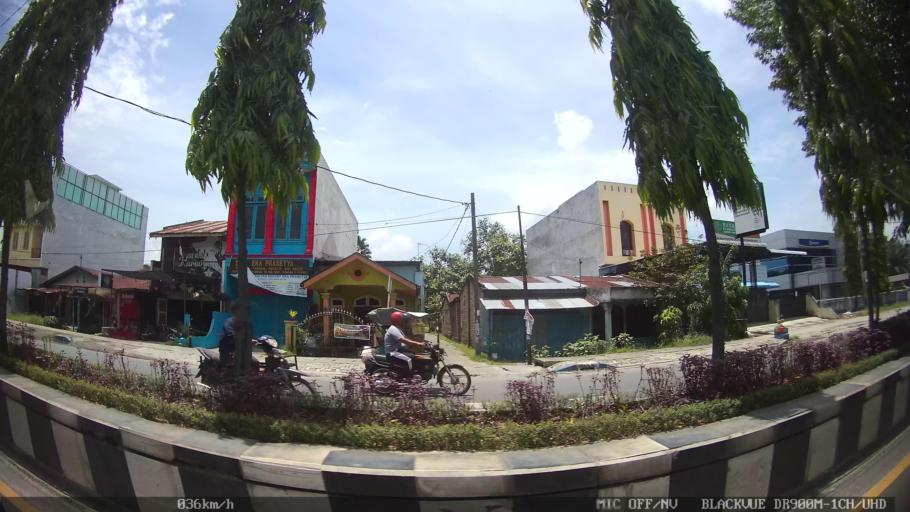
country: ID
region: North Sumatra
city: Percut
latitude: 3.5542
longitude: 98.8726
